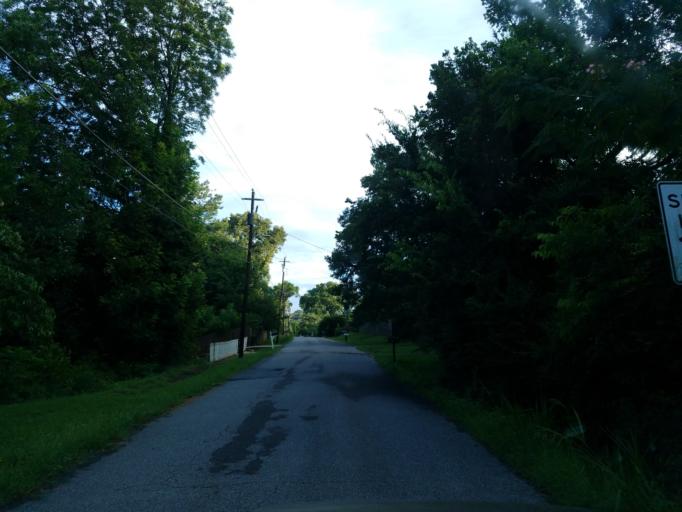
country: US
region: Georgia
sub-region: Bartow County
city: Emerson
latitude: 34.1288
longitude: -84.7583
